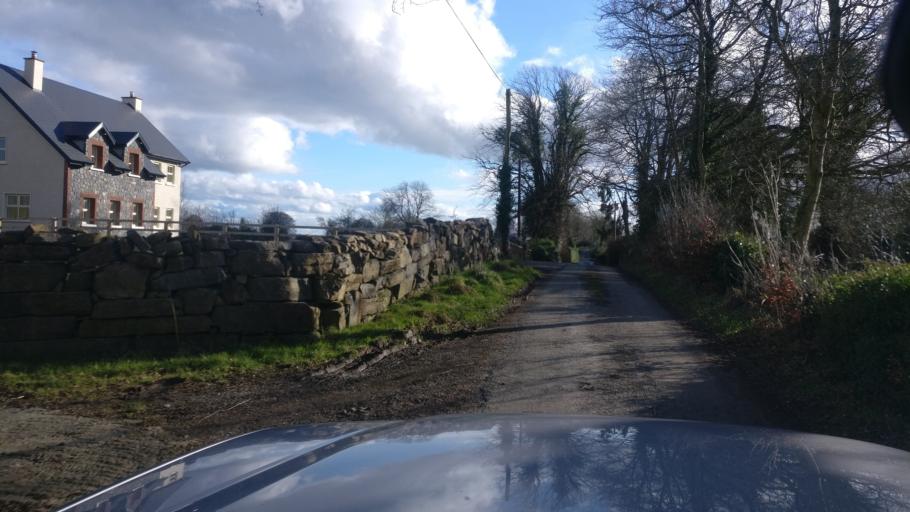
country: IE
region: Connaught
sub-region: County Galway
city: Loughrea
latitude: 53.1801
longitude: -8.4258
